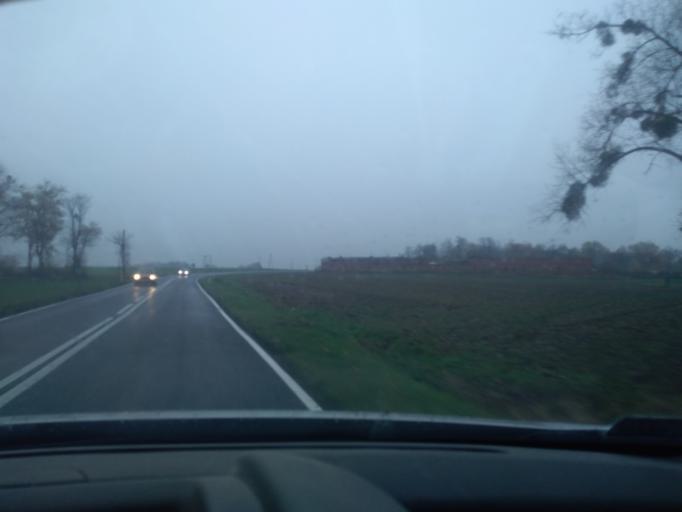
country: PL
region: Greater Poland Voivodeship
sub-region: Powiat poznanski
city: Murowana Goslina
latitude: 52.6418
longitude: 16.9345
